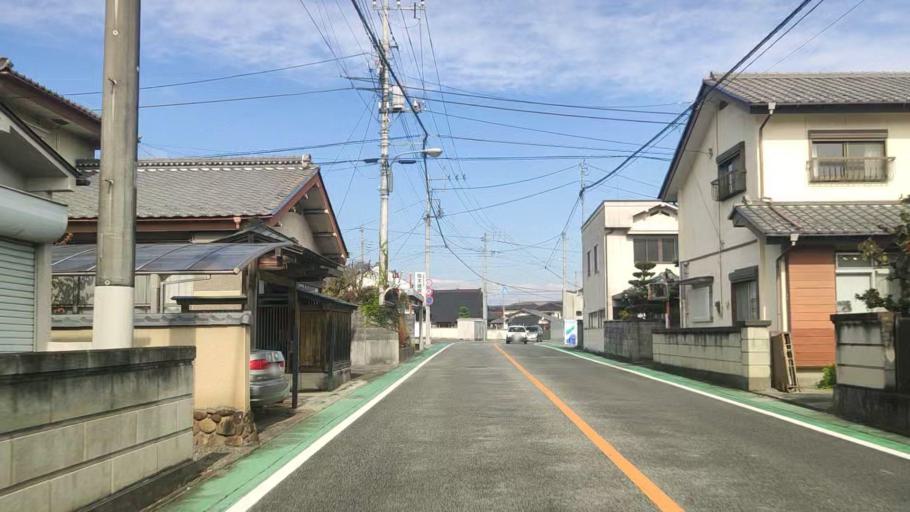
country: JP
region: Yamanashi
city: Ryuo
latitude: 35.5705
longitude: 138.4648
